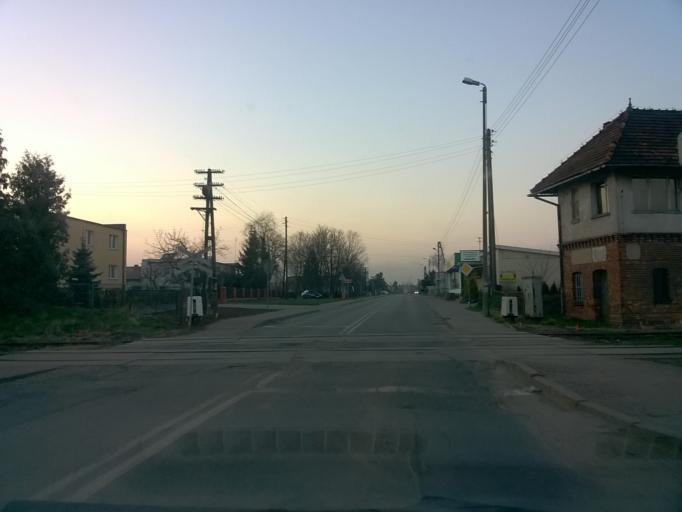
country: PL
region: Greater Poland Voivodeship
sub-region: Powiat wagrowiecki
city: Golancz
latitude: 52.9465
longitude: 17.3014
